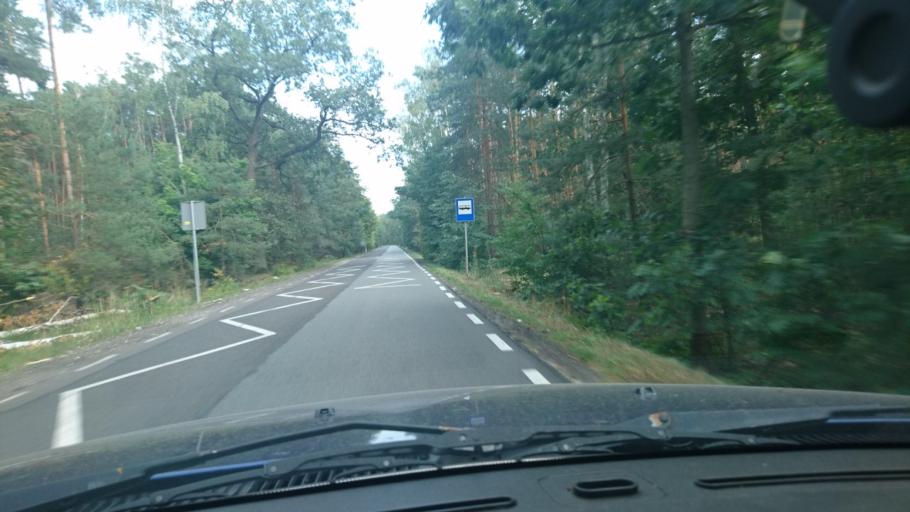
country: PL
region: Greater Poland Voivodeship
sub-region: Powiat ostrowski
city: Odolanow
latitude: 51.5375
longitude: 17.7325
